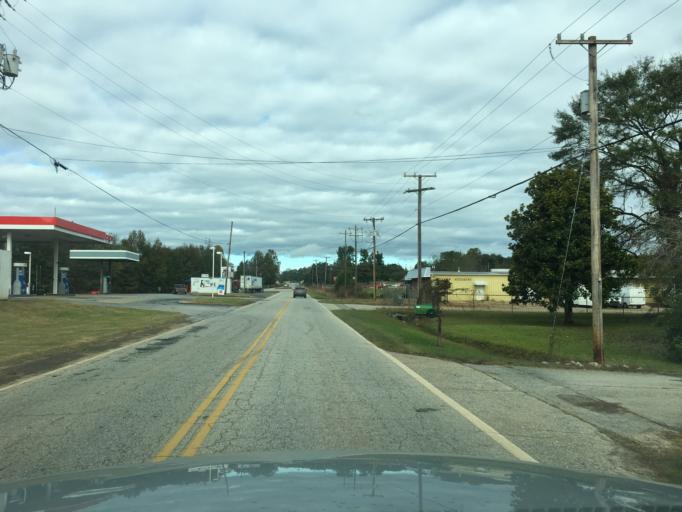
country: US
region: South Carolina
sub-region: Greenville County
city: Greer
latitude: 34.9909
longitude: -82.2442
